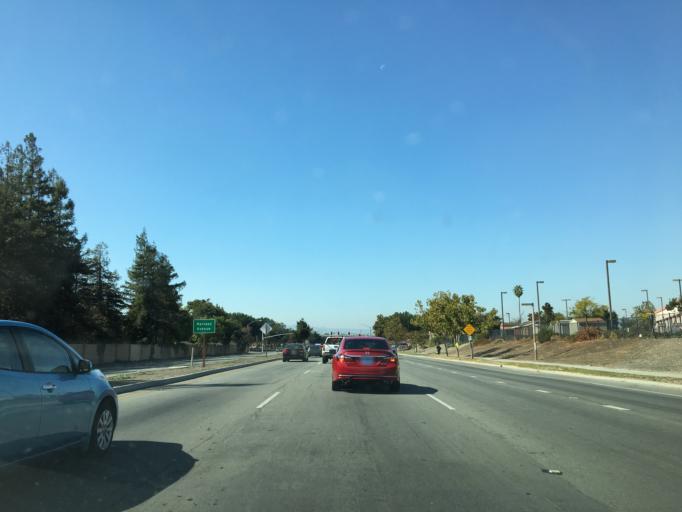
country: US
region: California
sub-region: Santa Clara County
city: Seven Trees
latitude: 37.2745
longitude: -121.8576
